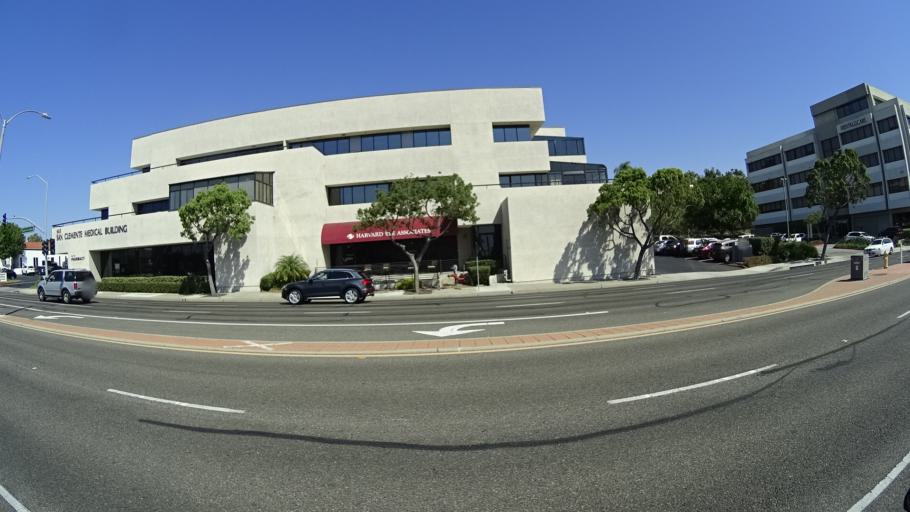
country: US
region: California
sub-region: Orange County
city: San Juan Capistrano
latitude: 33.4570
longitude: -117.6483
